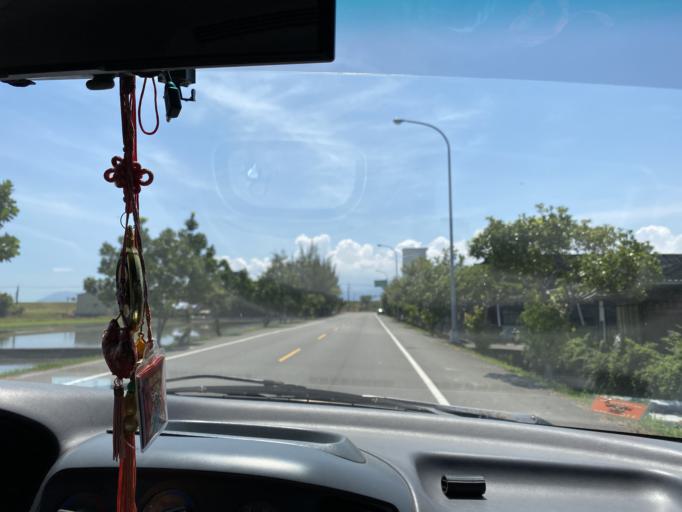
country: TW
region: Taiwan
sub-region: Yilan
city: Yilan
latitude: 24.7205
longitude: 121.8075
